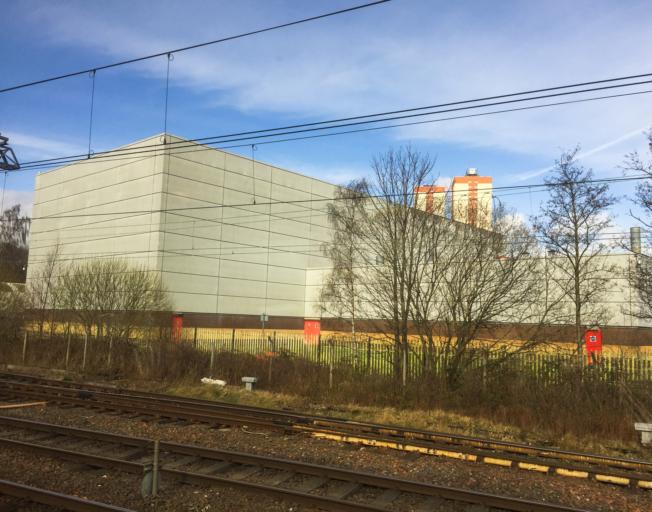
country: GB
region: Scotland
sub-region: East Dunbartonshire
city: Bishopbriggs
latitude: 55.8805
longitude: -4.2266
